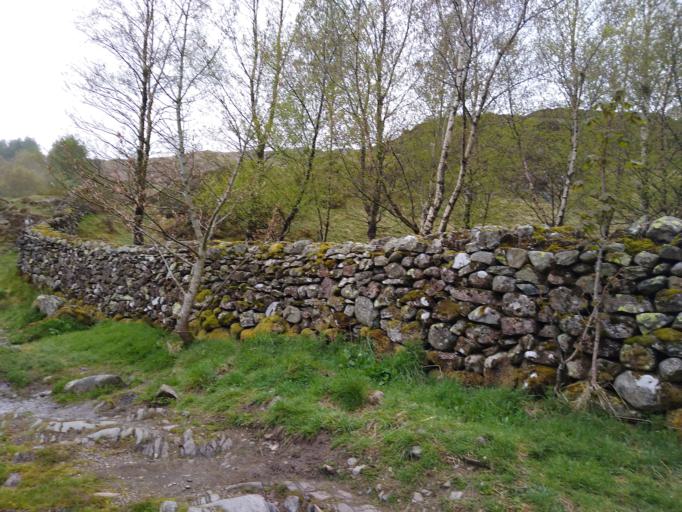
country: GB
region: England
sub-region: Cumbria
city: Keswick
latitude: 54.5371
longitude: -3.1216
